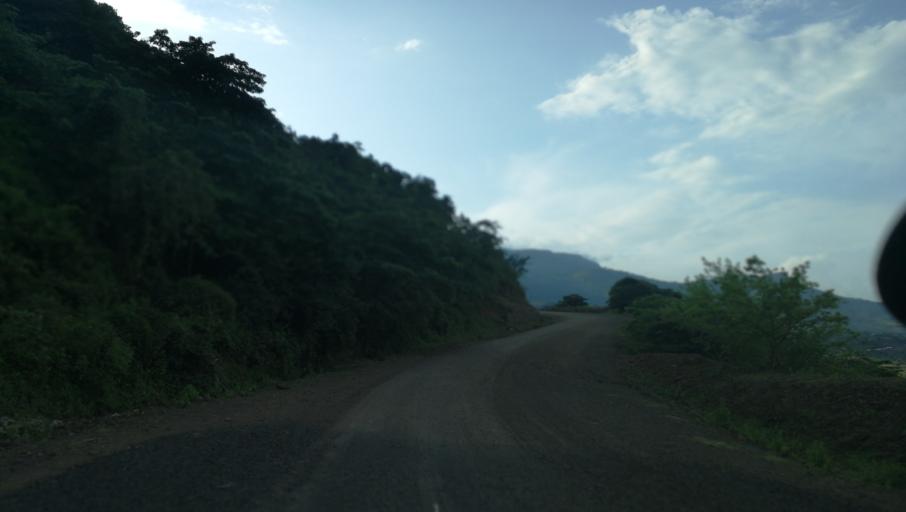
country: ET
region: Southern Nations, Nationalities, and People's Region
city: Areka
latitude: 6.8522
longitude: 37.2690
